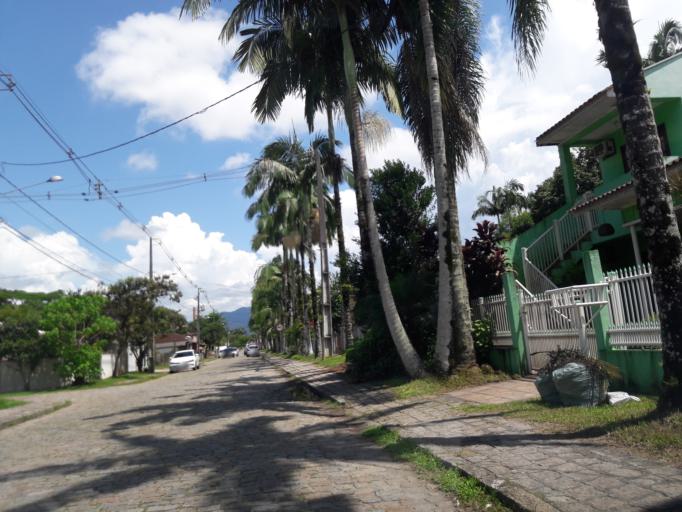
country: BR
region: Parana
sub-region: Antonina
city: Antonina
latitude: -25.4736
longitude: -48.8318
